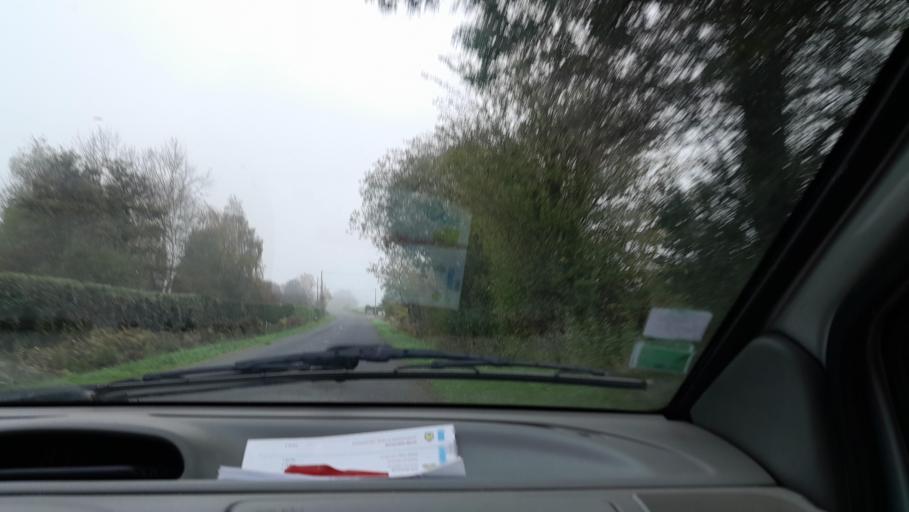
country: FR
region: Pays de la Loire
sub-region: Departement de la Mayenne
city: Saint-Pierre-la-Cour
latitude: 48.1324
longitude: -1.0236
